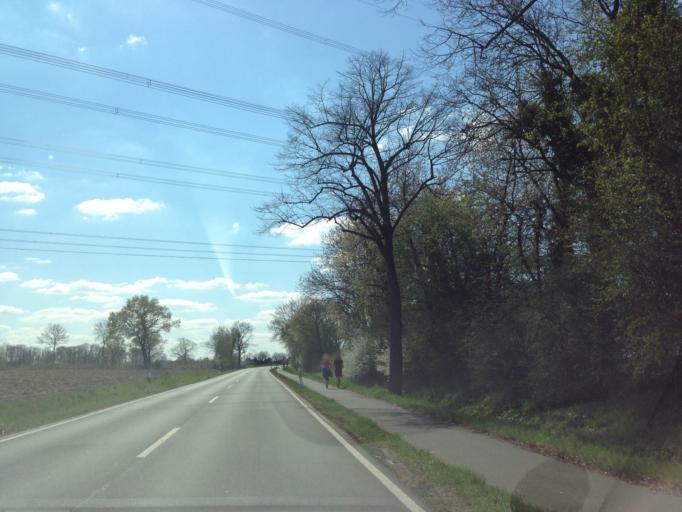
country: DE
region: North Rhine-Westphalia
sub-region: Regierungsbezirk Munster
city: Muenster
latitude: 51.9034
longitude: 7.5863
